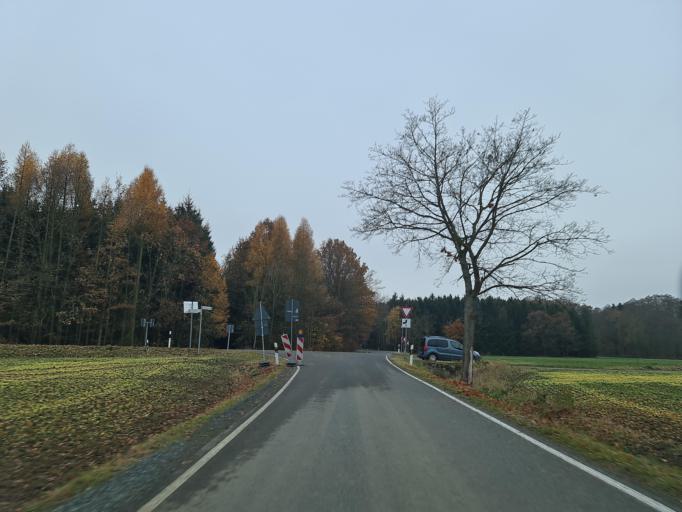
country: DE
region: Saxony
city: Syrau
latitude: 50.5143
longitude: 12.0795
